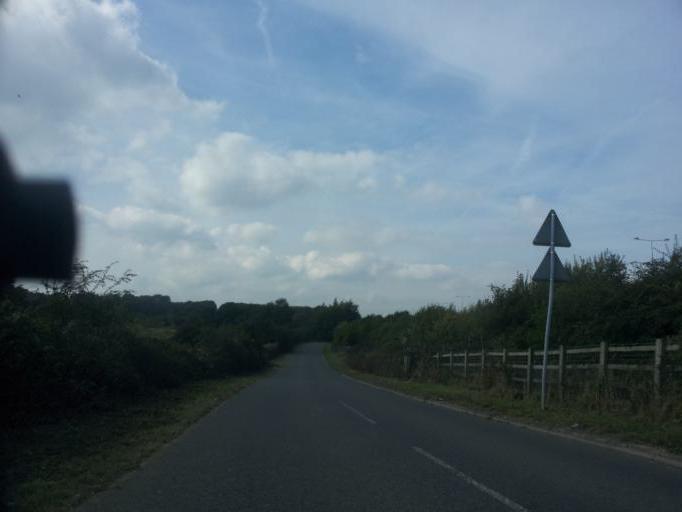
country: GB
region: England
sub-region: Kent
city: Boxley
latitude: 51.3246
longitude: 0.5466
